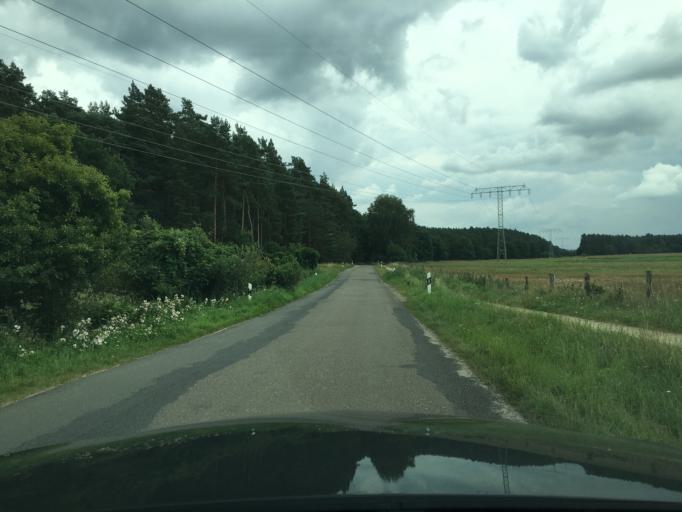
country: DE
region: Mecklenburg-Vorpommern
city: Mollenhagen
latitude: 53.4625
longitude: 12.8054
